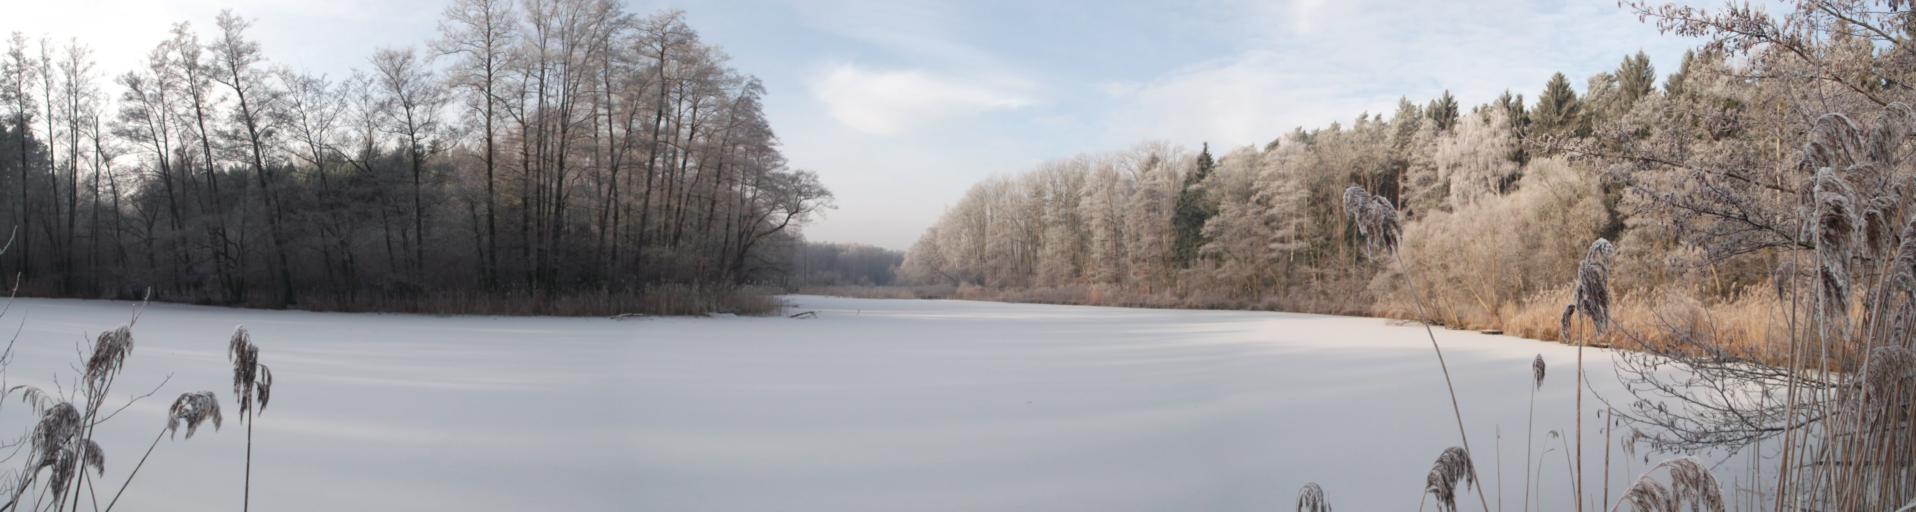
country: PL
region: Masovian Voivodeship
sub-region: Powiat piaseczynski
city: Tarczyn
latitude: 51.9664
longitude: 20.8028
